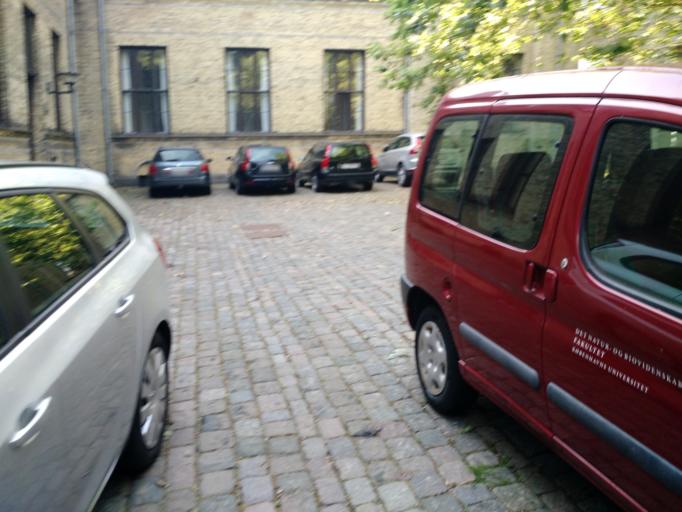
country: DK
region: Capital Region
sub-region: Frederiksberg Kommune
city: Frederiksberg
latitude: 55.6801
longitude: 12.5422
